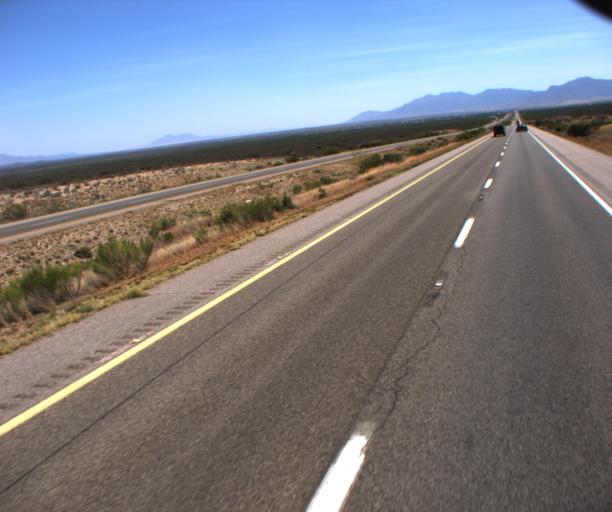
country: US
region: Arizona
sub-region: Cochise County
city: Huachuca City
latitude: 31.7636
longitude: -110.3503
